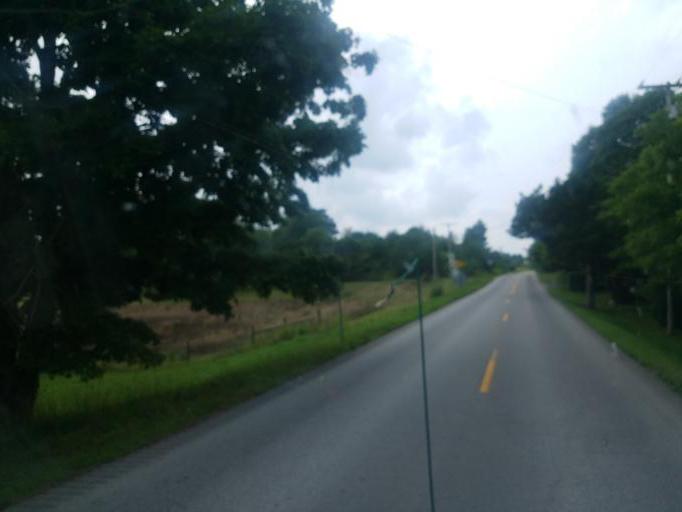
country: US
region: Kentucky
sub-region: Hart County
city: Munfordville
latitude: 37.3067
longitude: -86.0638
